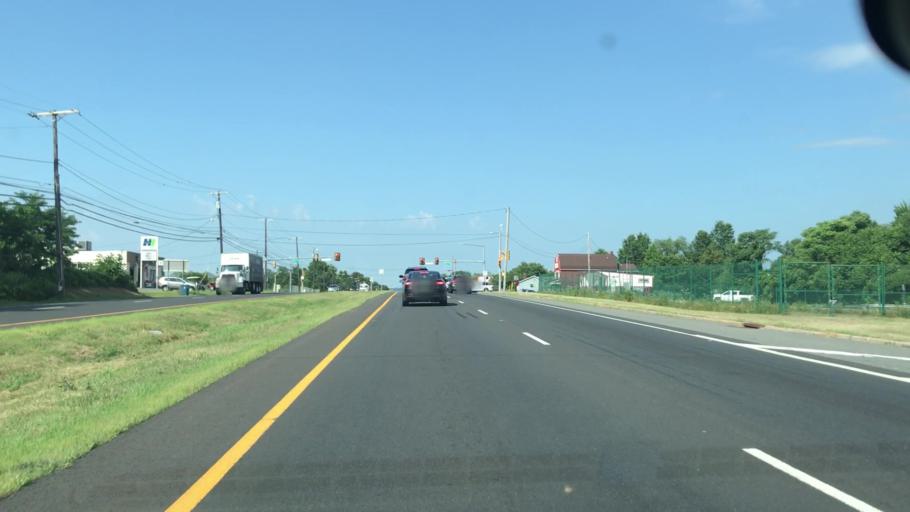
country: US
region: New Jersey
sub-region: Hunterdon County
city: Flemington
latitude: 40.5135
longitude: -74.8267
